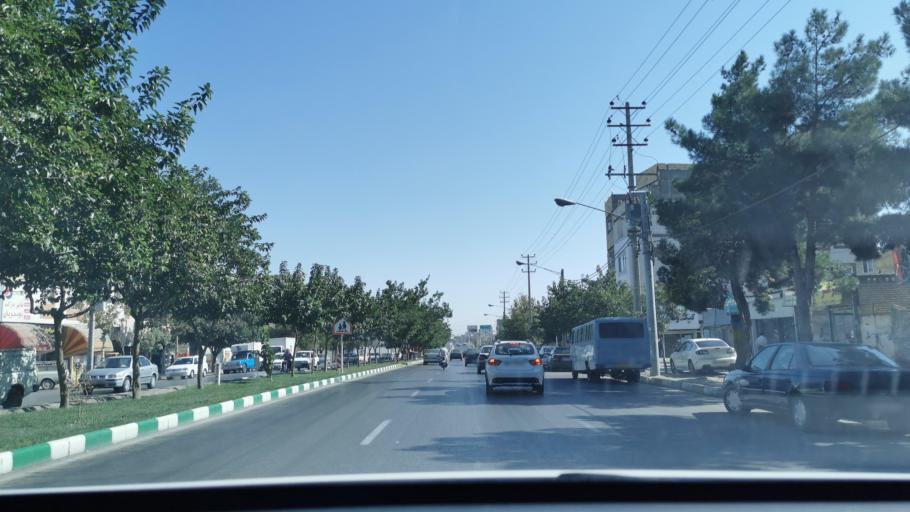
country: IR
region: Razavi Khorasan
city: Mashhad
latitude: 36.3332
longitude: 59.6023
